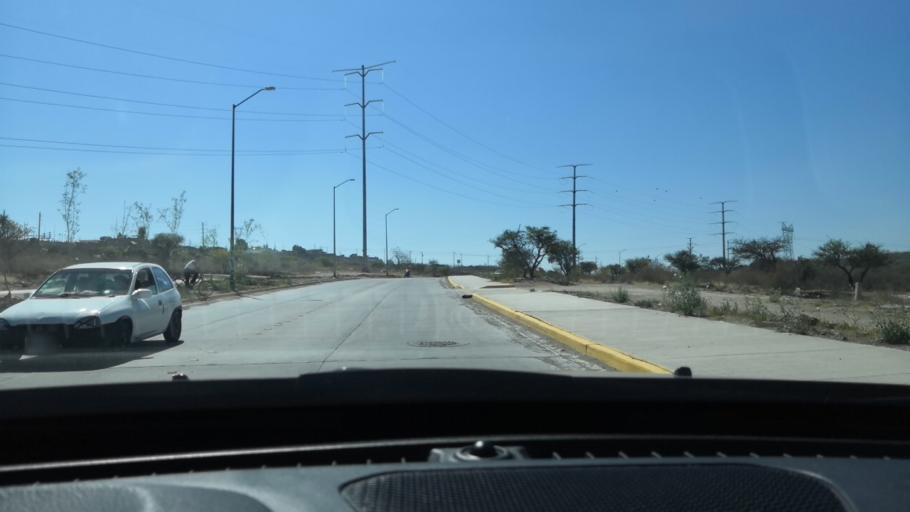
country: MX
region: Guanajuato
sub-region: Leon
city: Ejido la Joya
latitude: 21.1293
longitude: -101.7346
